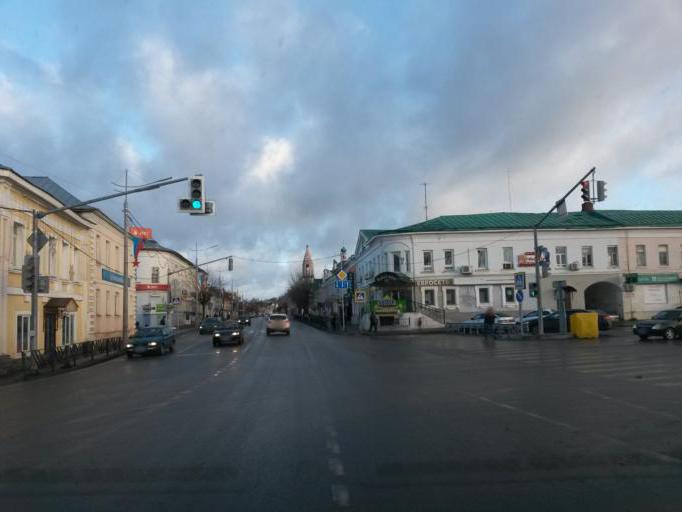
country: RU
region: Jaroslavl
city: Pereslavl'-Zalesskiy
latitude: 56.7388
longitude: 38.8559
